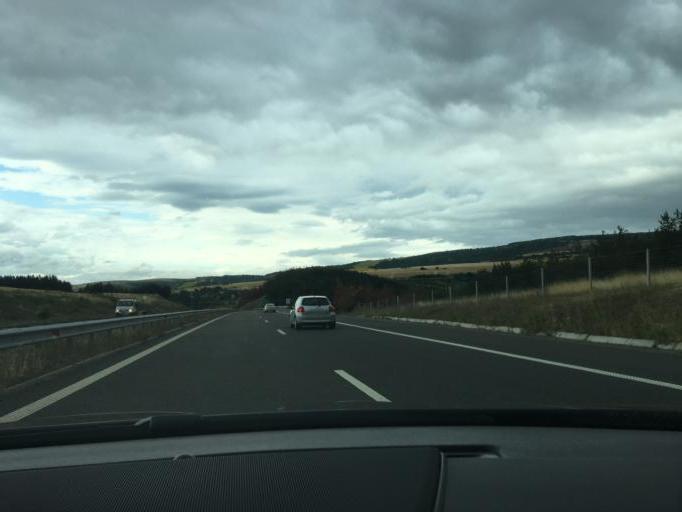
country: BG
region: Kyustendil
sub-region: Obshtina Dupnitsa
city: Dupnitsa
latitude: 42.3271
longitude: 23.0978
